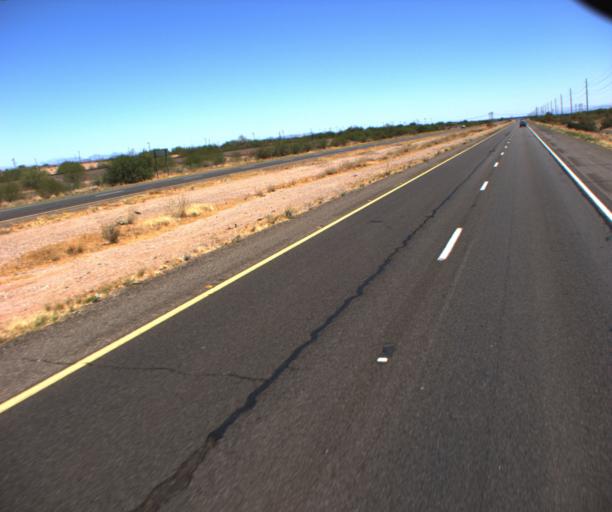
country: US
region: Arizona
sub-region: Maricopa County
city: Sun City West
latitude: 33.7028
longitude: -112.4326
